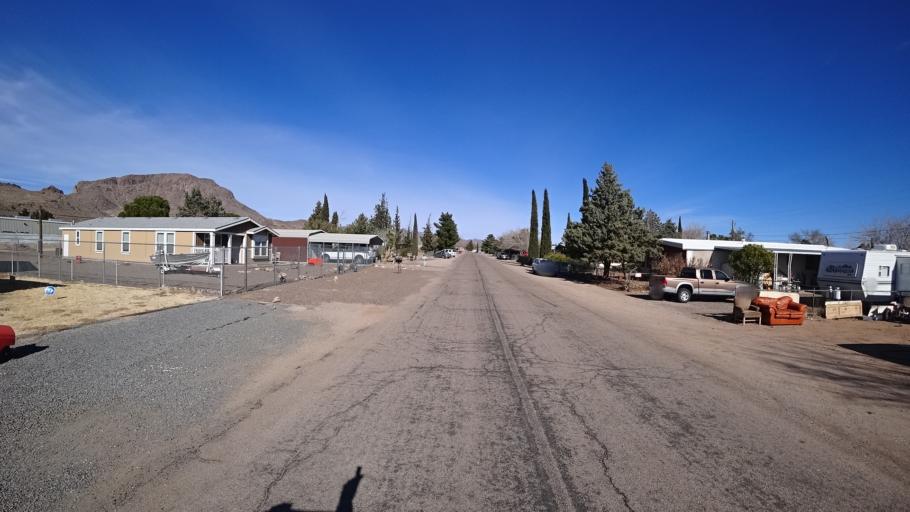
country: US
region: Arizona
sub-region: Mohave County
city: New Kingman-Butler
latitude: 35.2622
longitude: -114.0383
